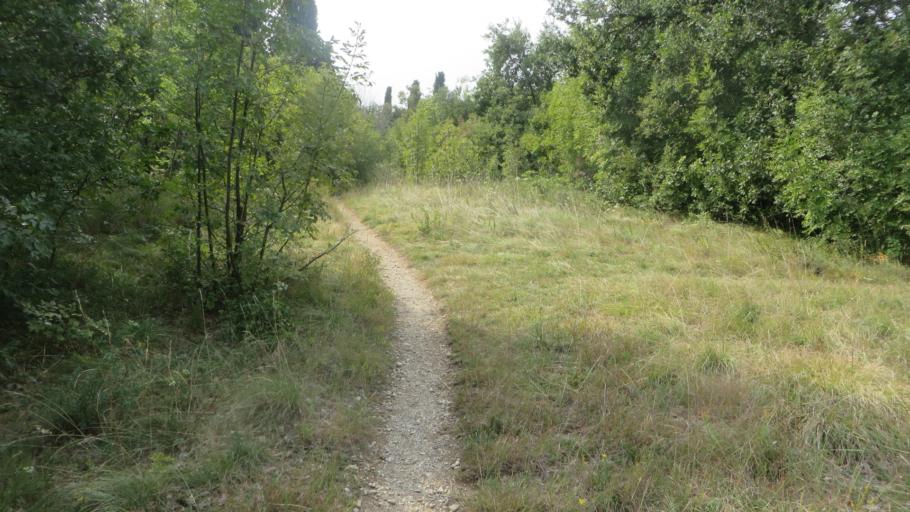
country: IT
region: Lombardy
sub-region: Provincia di Brescia
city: Solarolo
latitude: 45.5479
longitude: 10.5731
